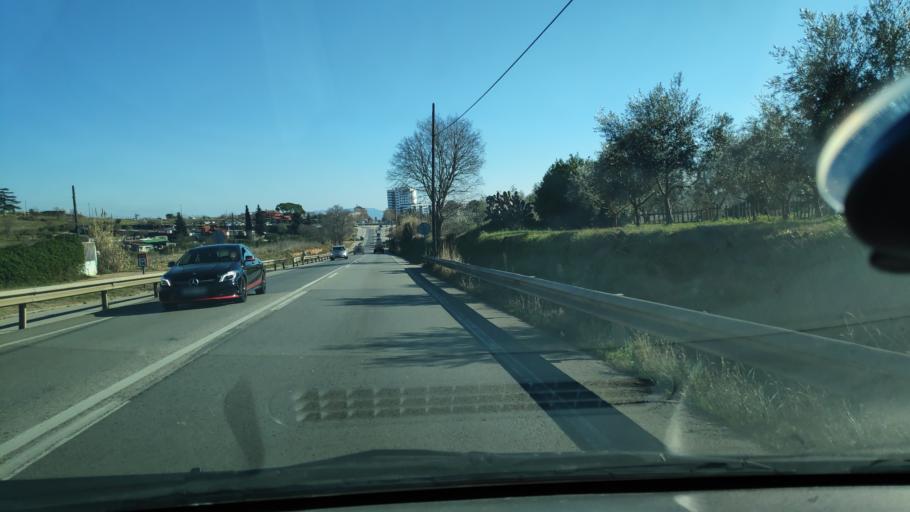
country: ES
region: Catalonia
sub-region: Provincia de Barcelona
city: Sant Quirze del Valles
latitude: 41.5522
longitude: 2.0708
